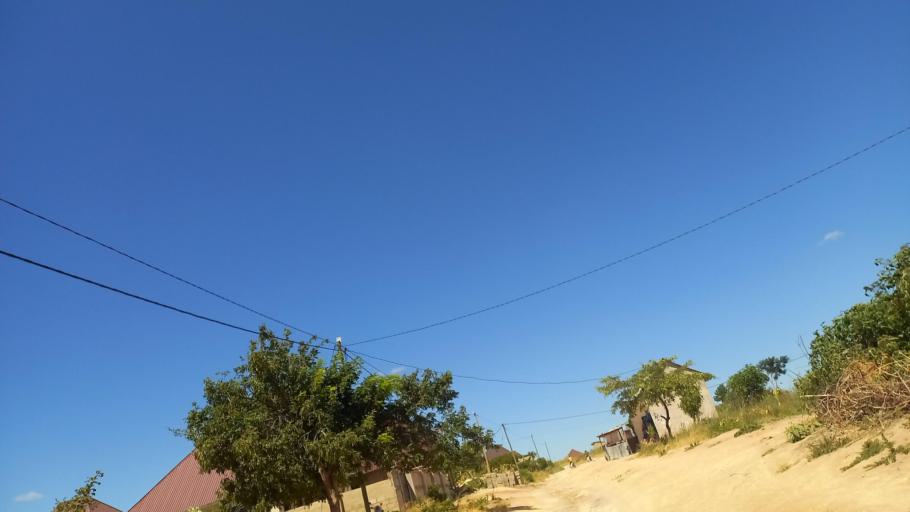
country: TZ
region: Dodoma
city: Dodoma
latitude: -6.1305
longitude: 35.6963
